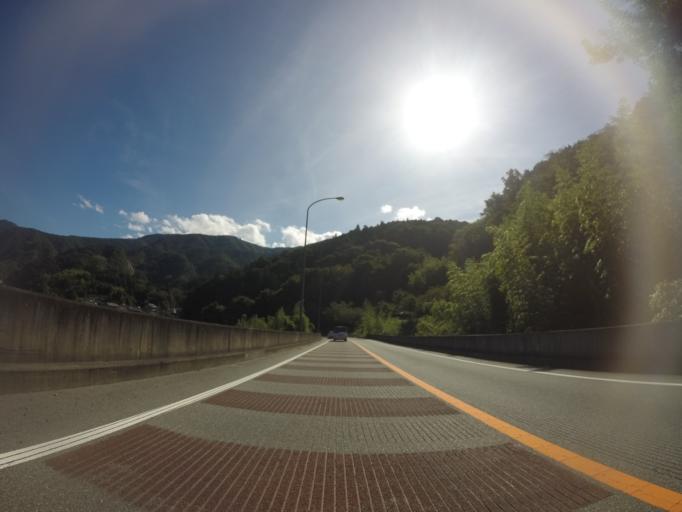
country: JP
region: Shizuoka
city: Fujinomiya
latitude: 35.3554
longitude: 138.4515
